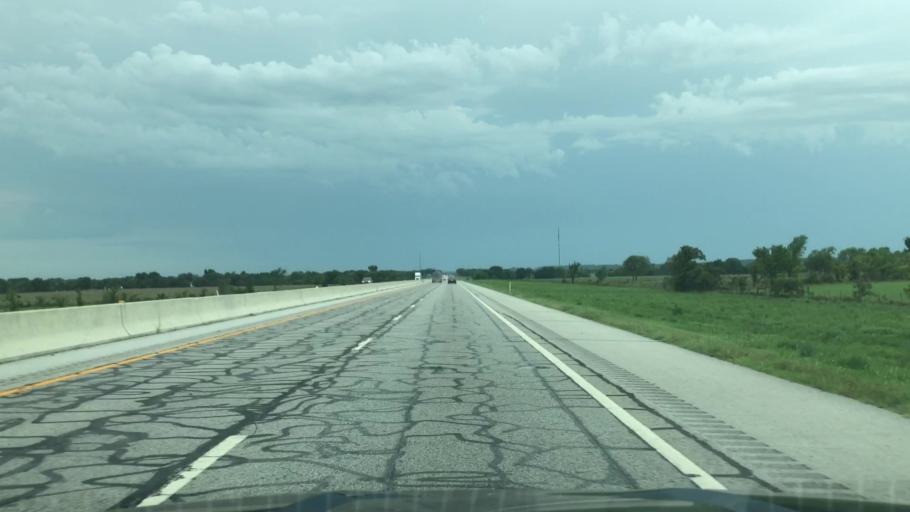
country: US
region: Oklahoma
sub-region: Craig County
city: Vinita
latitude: 36.5193
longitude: -95.2607
